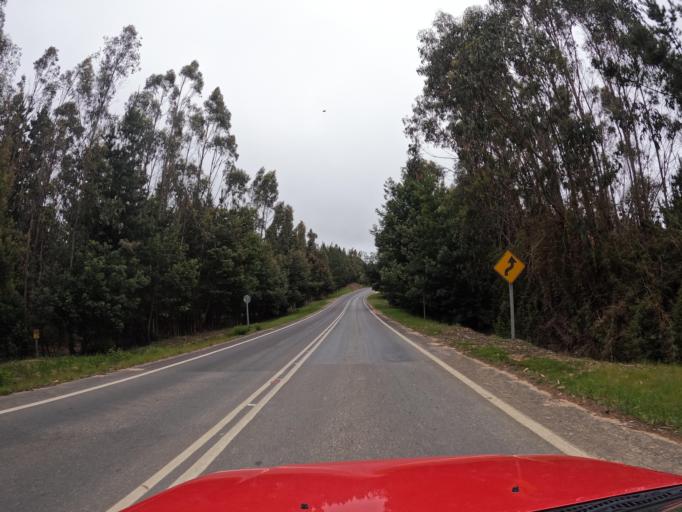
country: CL
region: O'Higgins
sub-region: Provincia de Colchagua
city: Santa Cruz
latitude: -34.6063
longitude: -72.0149
